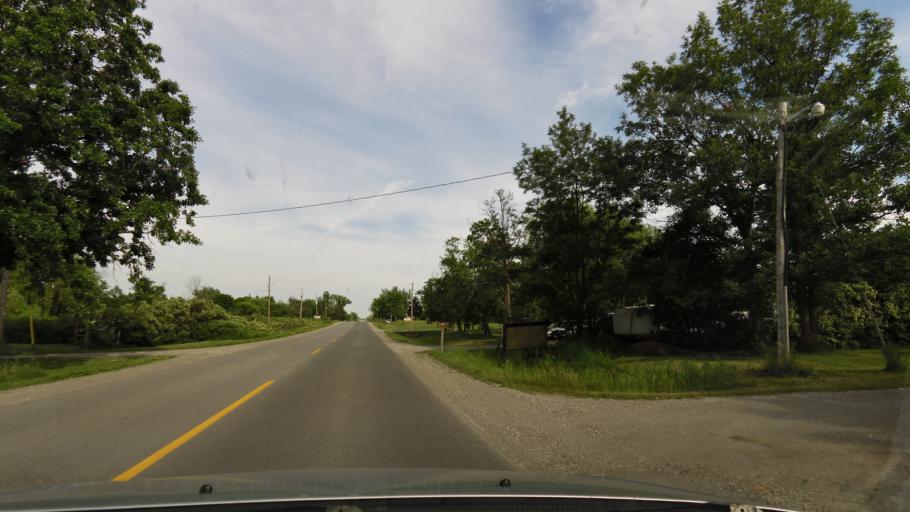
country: CA
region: Ontario
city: Ancaster
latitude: 43.0381
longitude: -80.0349
